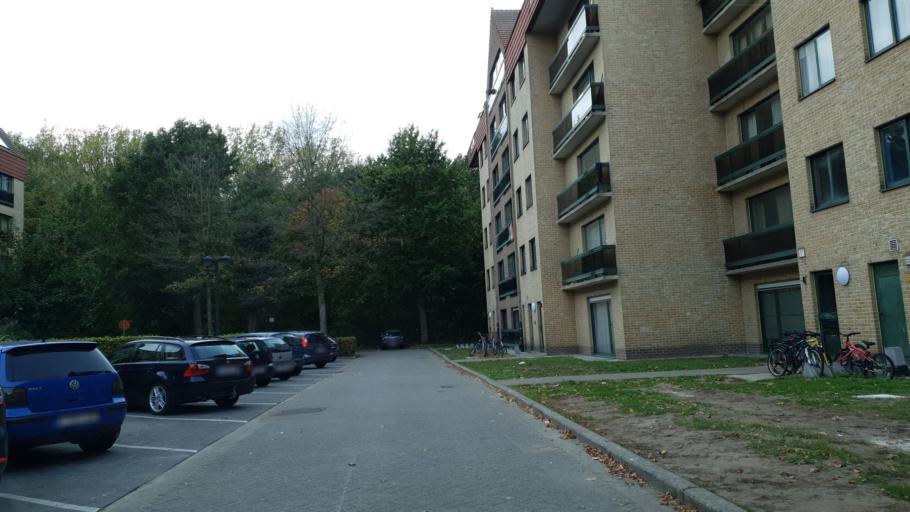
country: BE
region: Flanders
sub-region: Provincie Antwerpen
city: Antwerpen
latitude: 51.2268
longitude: 4.3760
